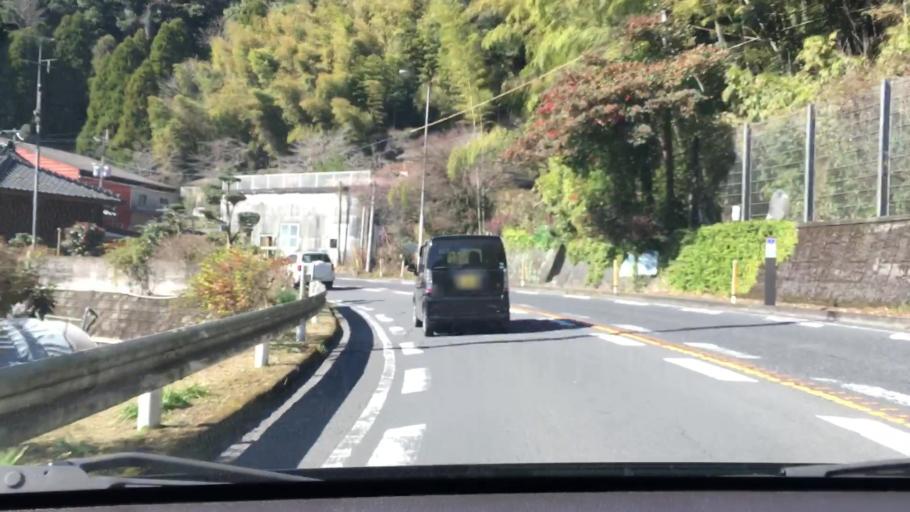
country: JP
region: Kagoshima
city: Kagoshima-shi
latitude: 31.6533
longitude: 130.5068
